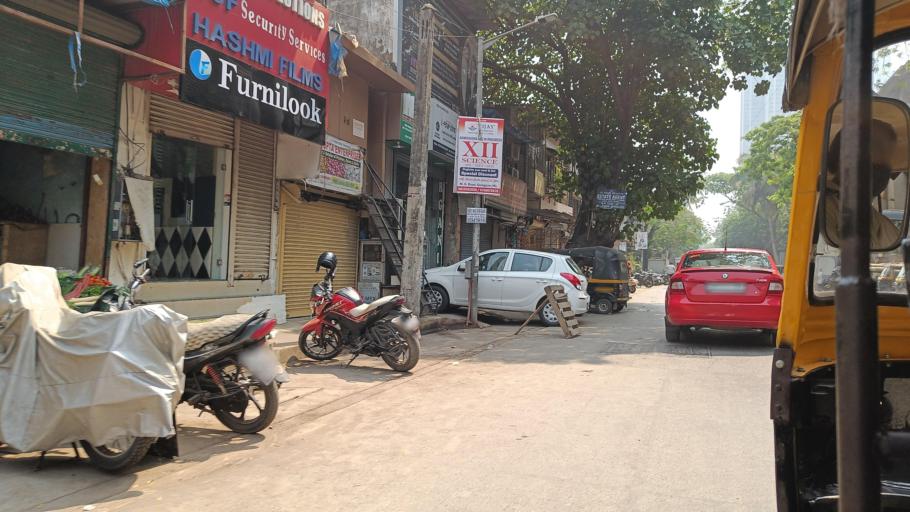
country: IN
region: Maharashtra
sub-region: Mumbai Suburban
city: Powai
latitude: 19.1555
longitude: 72.8363
